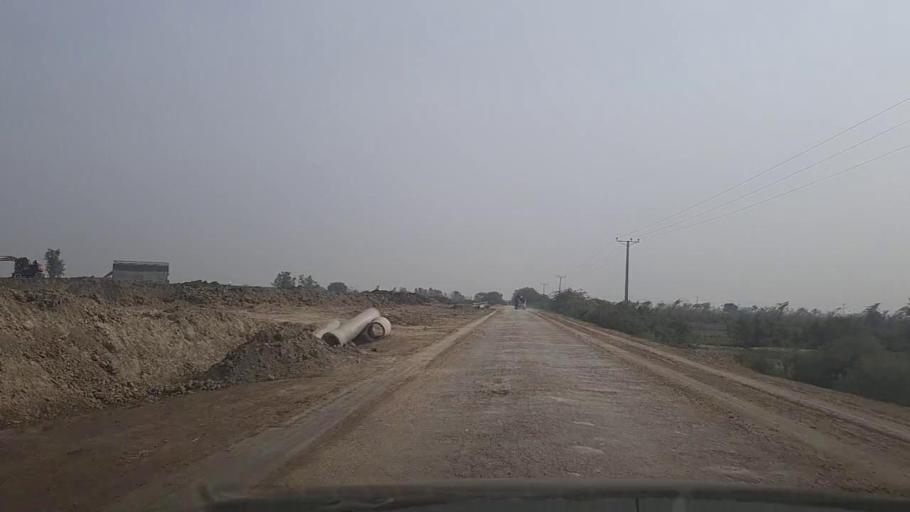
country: PK
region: Sindh
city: Mirpur Sakro
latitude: 24.4746
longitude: 67.6672
